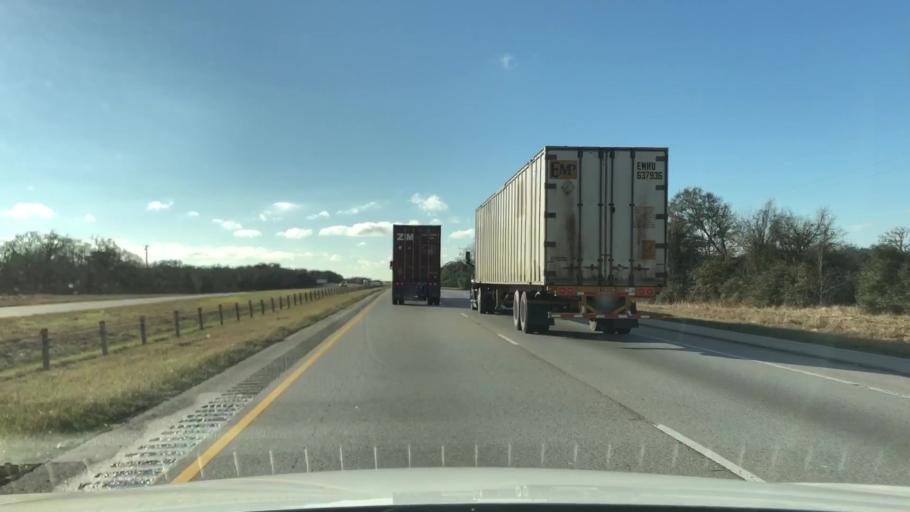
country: US
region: Texas
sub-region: Colorado County
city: Weimar
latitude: 29.6910
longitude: -96.6602
